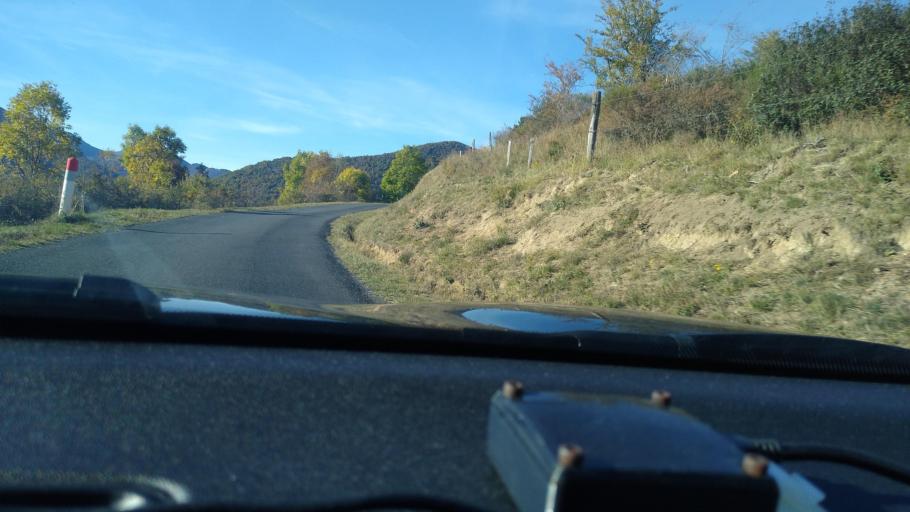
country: FR
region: Languedoc-Roussillon
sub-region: Departement de l'Aude
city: Quillan
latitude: 42.7290
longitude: 2.1171
